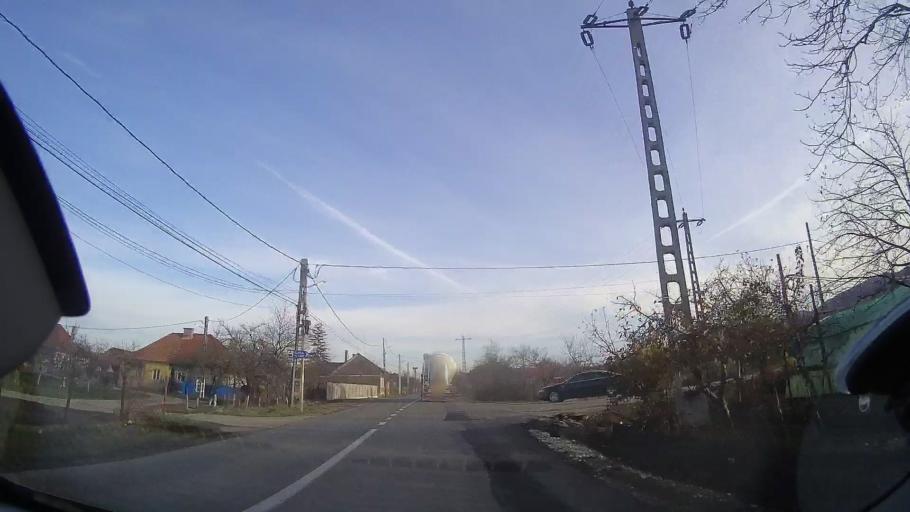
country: RO
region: Bihor
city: Lugasu de Jos
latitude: 47.0424
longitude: 22.3564
